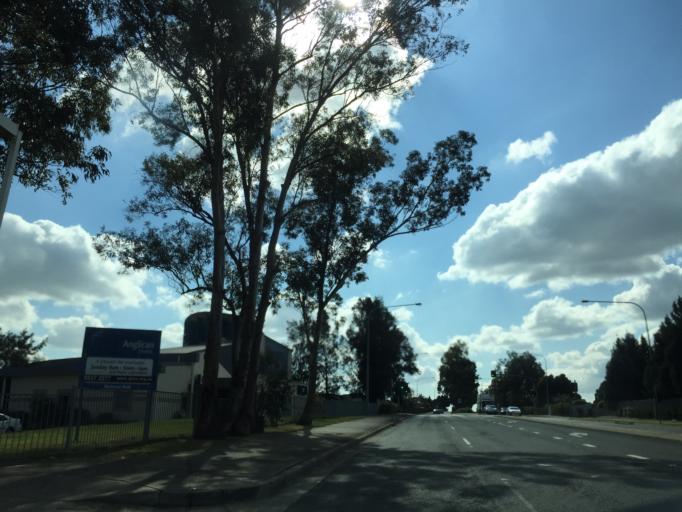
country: AU
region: New South Wales
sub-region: Blacktown
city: Quakers Hill
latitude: -33.7173
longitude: 150.8925
